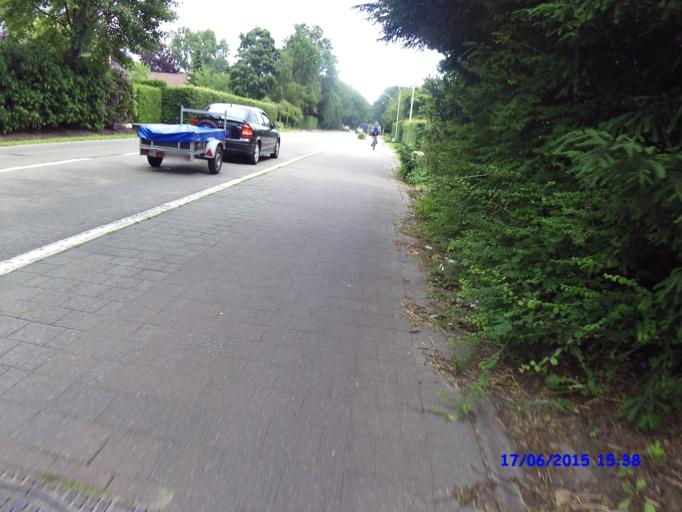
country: BE
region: Flanders
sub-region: Provincie Antwerpen
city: Aartselaar
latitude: 51.1441
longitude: 4.4024
